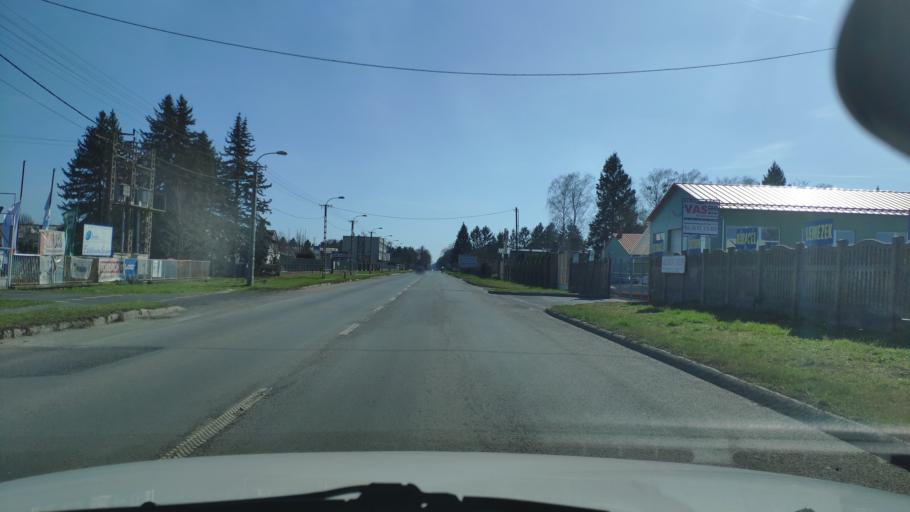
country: HU
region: Zala
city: Nagykanizsa
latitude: 46.4335
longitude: 16.9877
